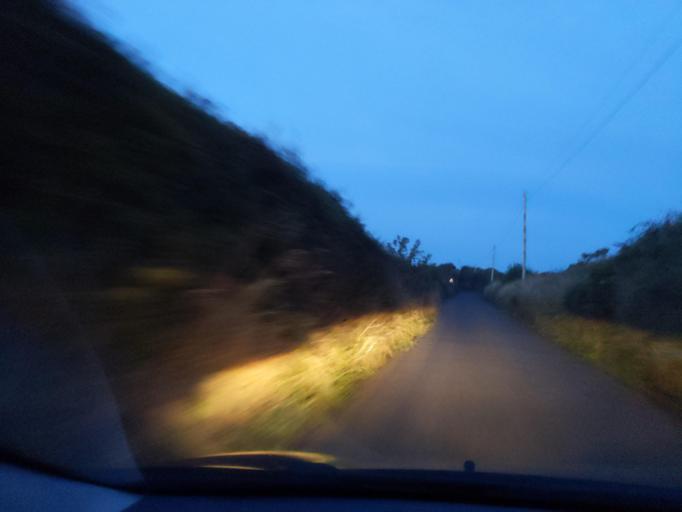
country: GB
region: England
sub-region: Cornwall
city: Camelford
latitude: 50.6973
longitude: -4.6633
